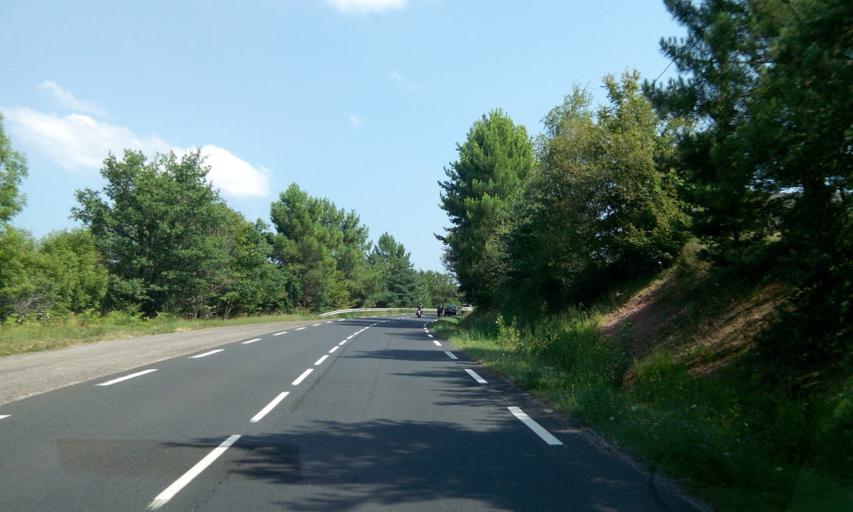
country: FR
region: Limousin
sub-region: Departement de la Correze
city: Cosnac
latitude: 45.1112
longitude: 1.5644
